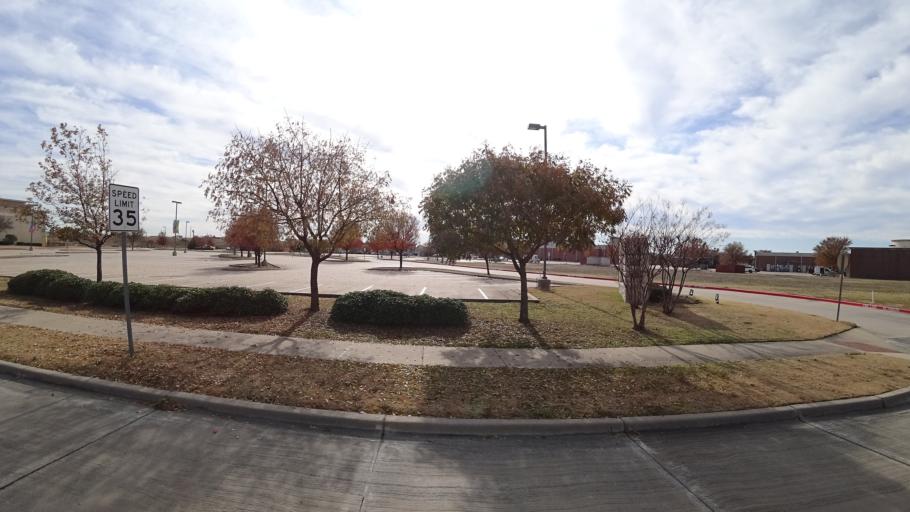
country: US
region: Texas
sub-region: Denton County
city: Lewisville
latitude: 33.0252
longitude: -96.9361
